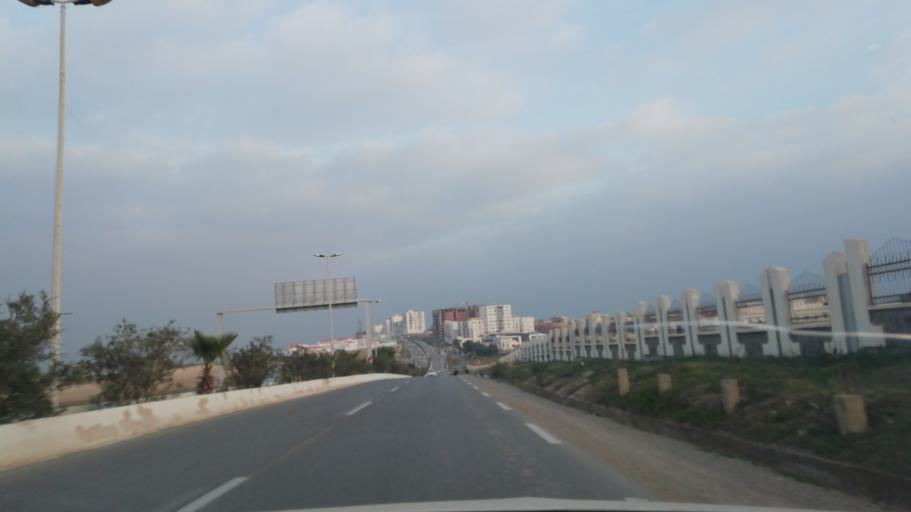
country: DZ
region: Sidi Bel Abbes
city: Sidi Bel Abbes
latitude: 35.2250
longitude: -0.6345
